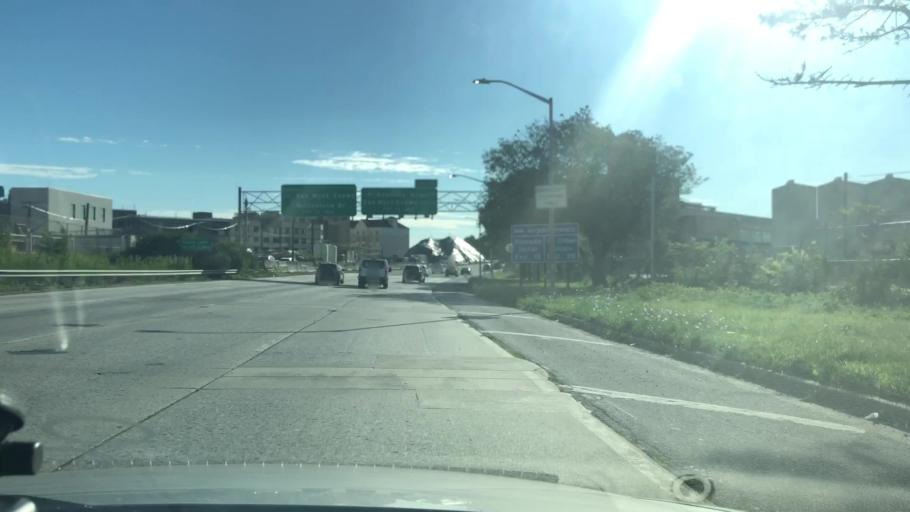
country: US
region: New York
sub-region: Queens County
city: Jamaica
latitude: 40.6639
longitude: -73.8099
